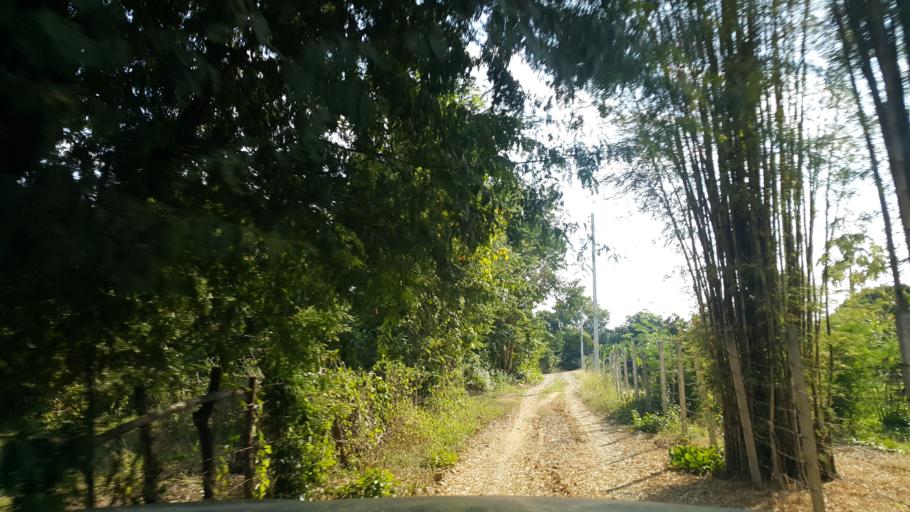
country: TH
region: Lamphun
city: Ban Thi
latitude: 18.5656
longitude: 99.1232
